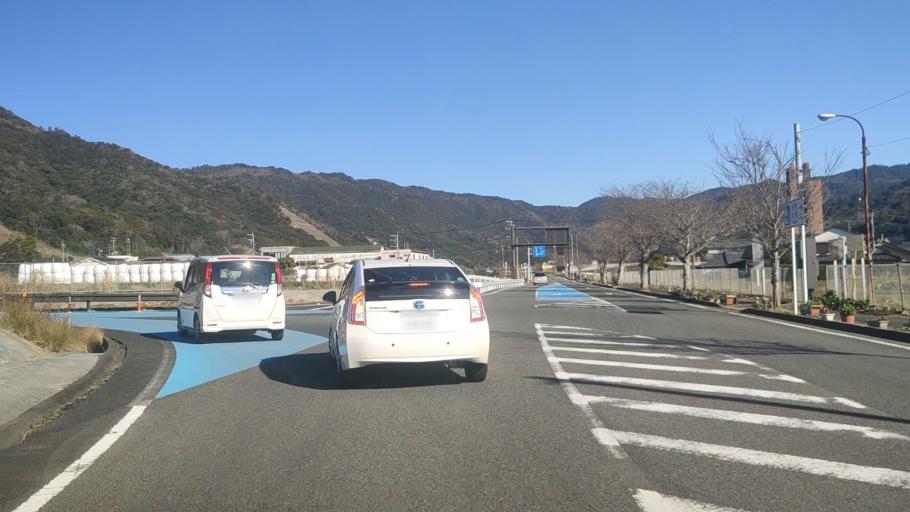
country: JP
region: Miyazaki
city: Nobeoka
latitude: 32.7099
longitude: 131.8198
